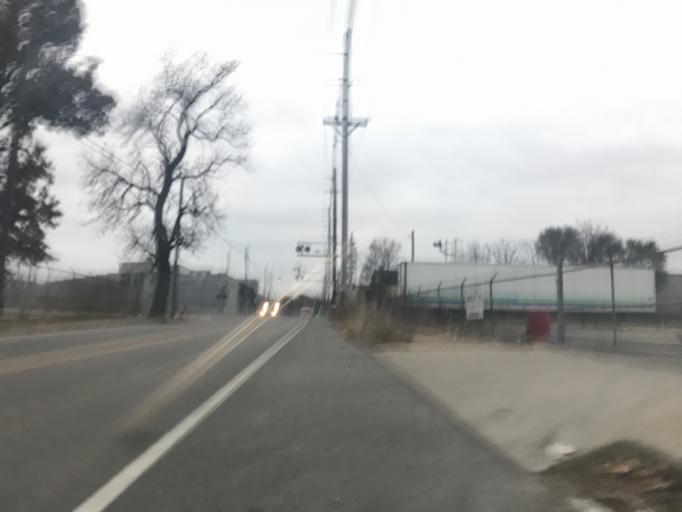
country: US
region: Kentucky
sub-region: Jefferson County
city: Louisville
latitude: 38.2309
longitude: -85.7746
